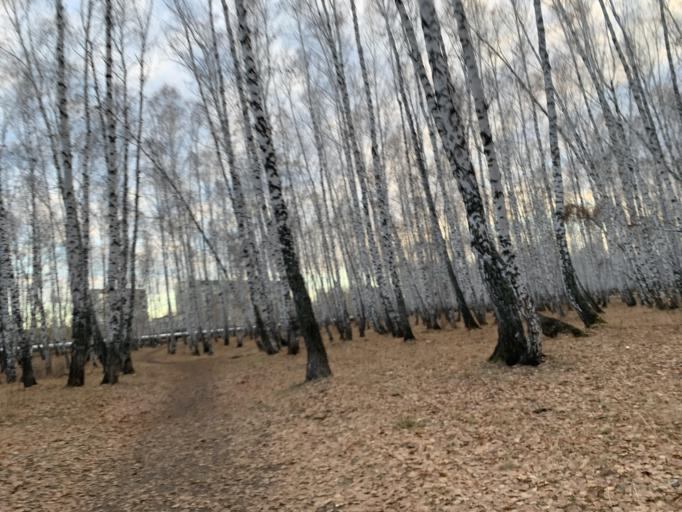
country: RU
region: Chelyabinsk
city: Roshchino
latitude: 55.2044
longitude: 61.3123
